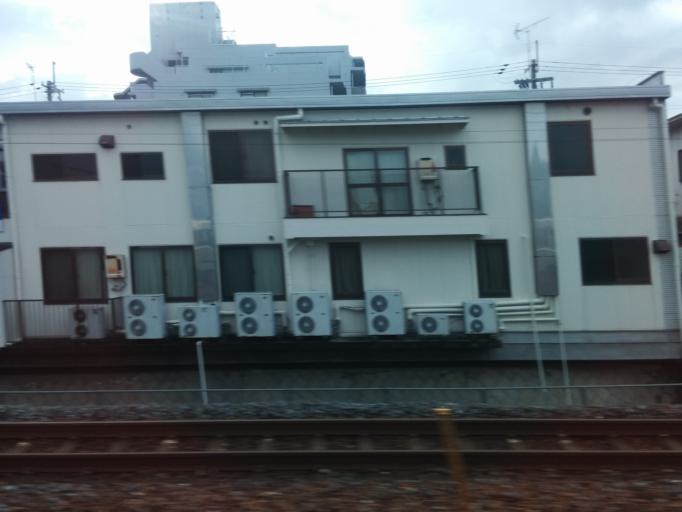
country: JP
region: Shiga Prefecture
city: Otsu-shi
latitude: 34.9831
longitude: 135.9189
